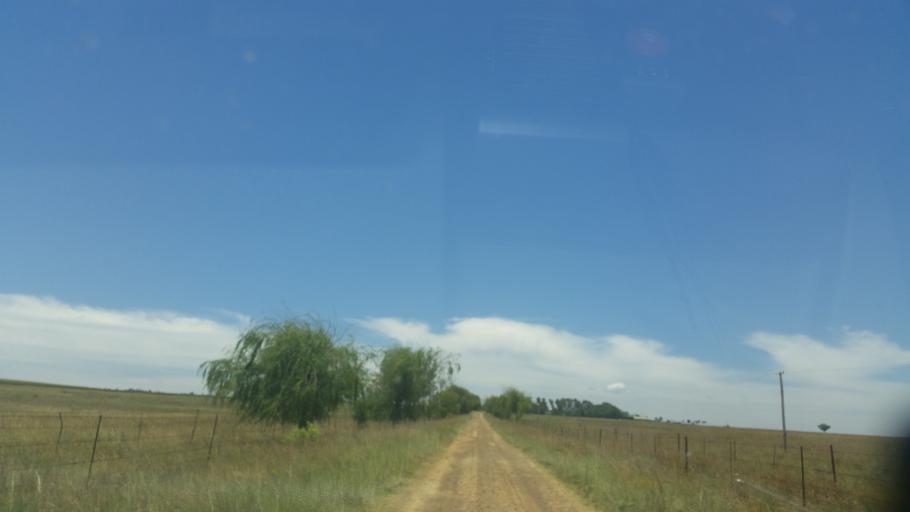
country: ZA
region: Orange Free State
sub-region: Thabo Mofutsanyana District Municipality
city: Harrismith
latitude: -28.1863
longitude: 29.0199
